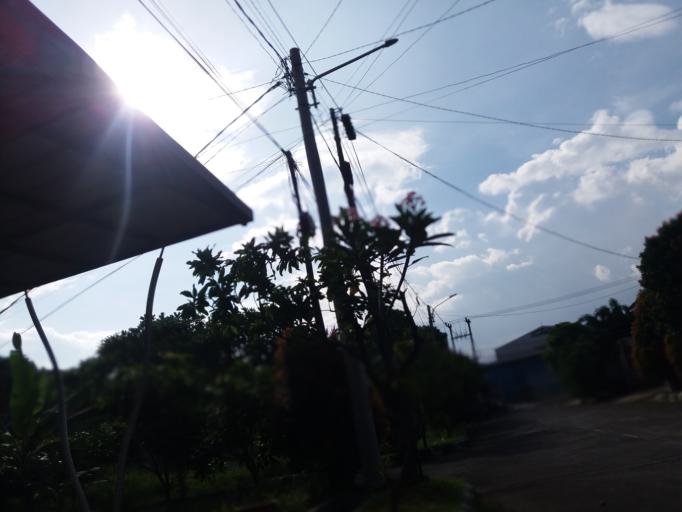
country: ID
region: West Java
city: Bandung
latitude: -6.9281
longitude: 107.6674
